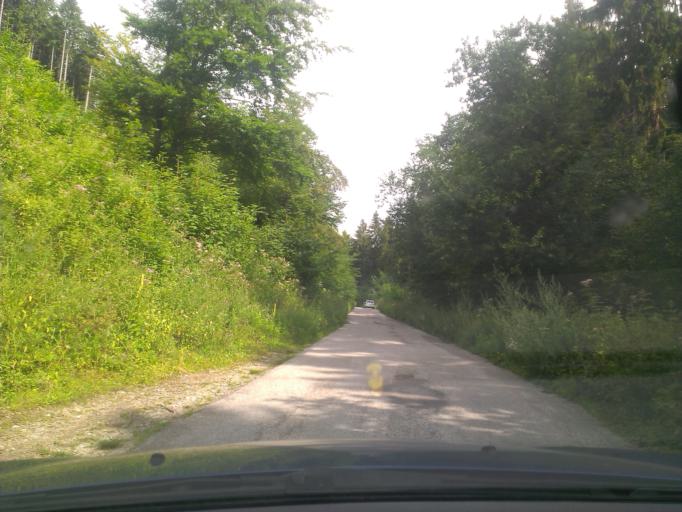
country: SK
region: Zilinsky
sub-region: Okres Zilina
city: Vrutky
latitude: 49.1073
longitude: 18.8891
